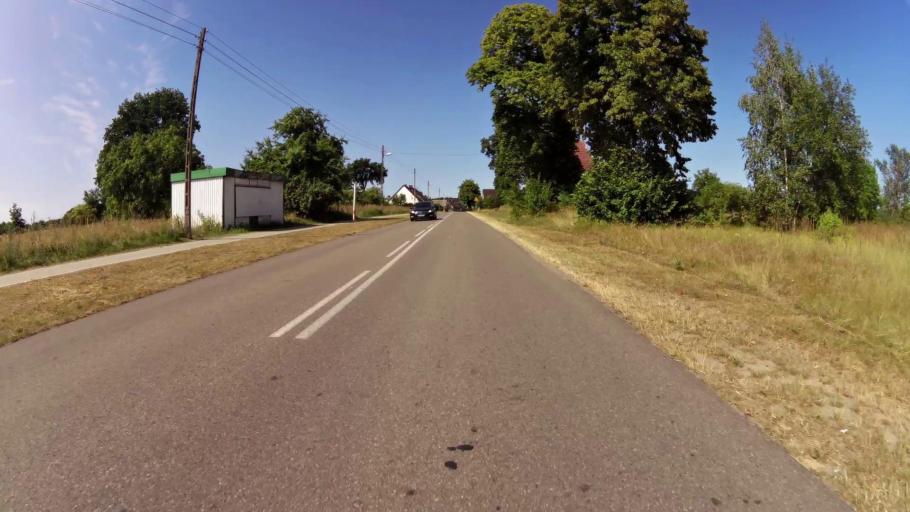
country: PL
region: West Pomeranian Voivodeship
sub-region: Powiat stargardzki
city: Dobrzany
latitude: 53.3435
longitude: 15.3949
